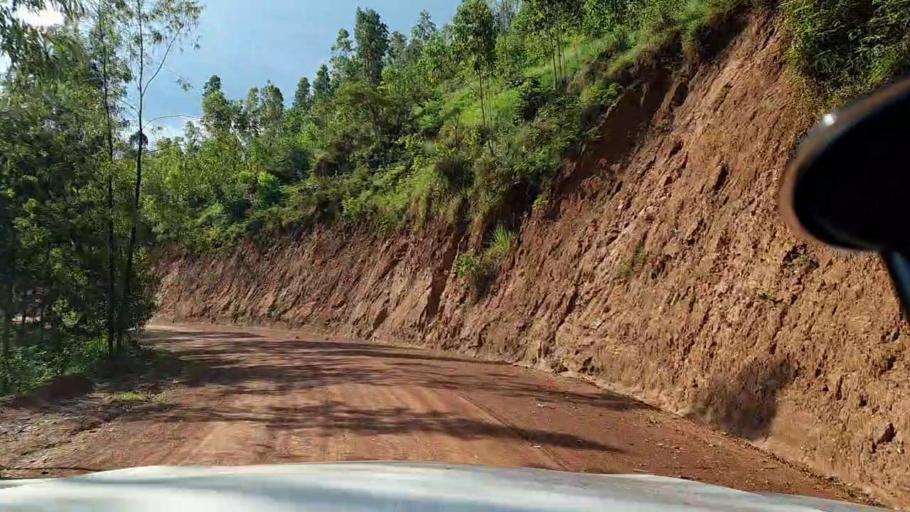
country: RW
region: Kigali
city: Kigali
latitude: -1.8447
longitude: 29.8606
